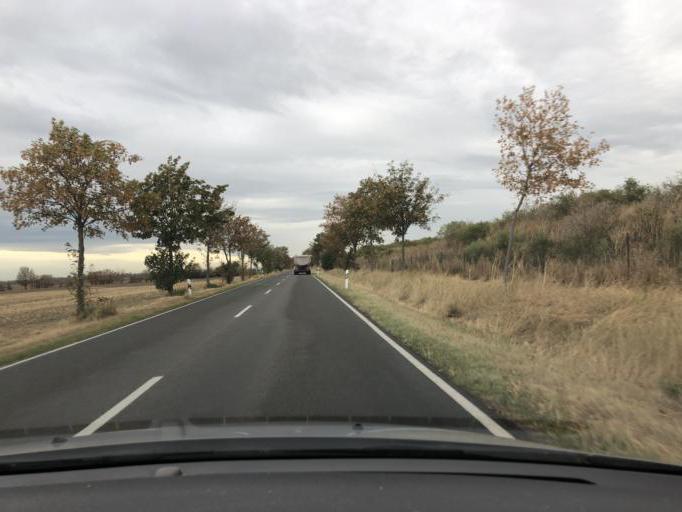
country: DE
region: Saxony-Anhalt
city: Nienburg/Saale
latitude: 51.8437
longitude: 11.7391
